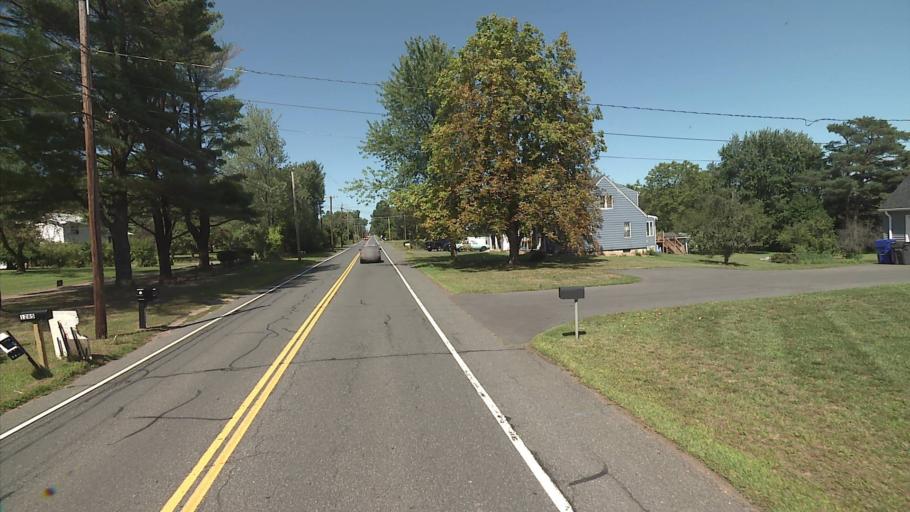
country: US
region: Connecticut
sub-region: Hartford County
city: Thompsonville
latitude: 42.0131
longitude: -72.6161
